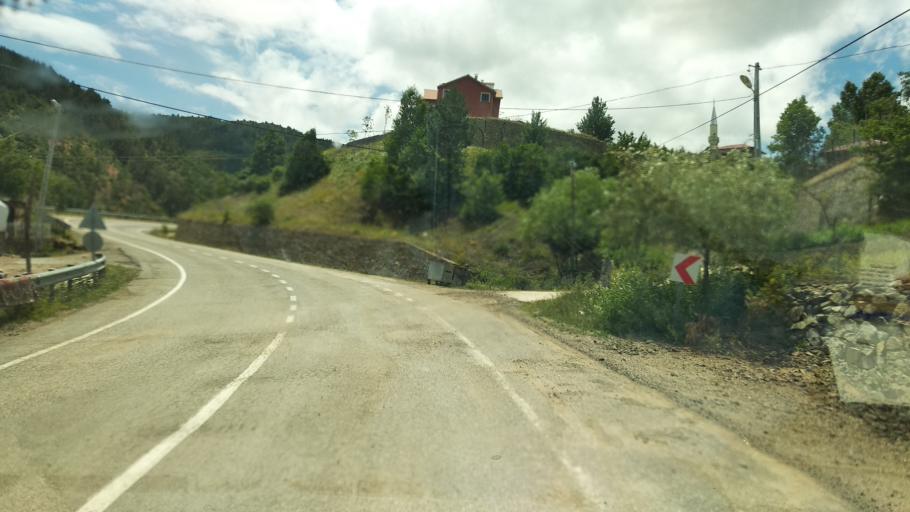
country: TR
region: Gumushane
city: Kose
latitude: 40.3077
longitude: 39.5580
